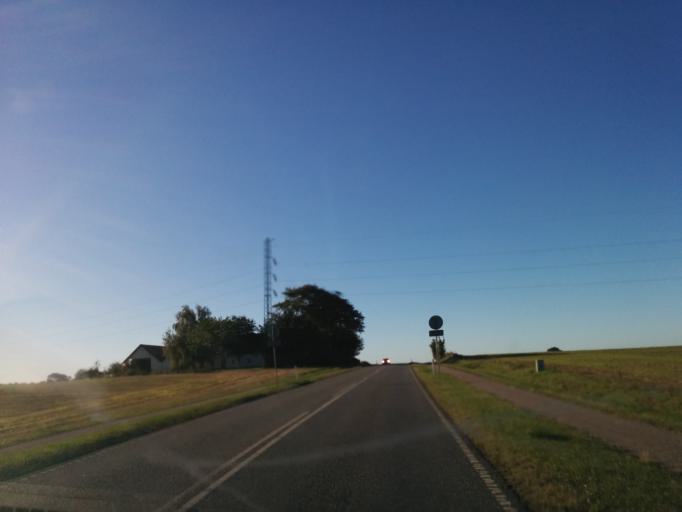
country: DK
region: South Denmark
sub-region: Kolding Kommune
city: Sonder Bjert
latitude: 55.4493
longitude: 9.5572
